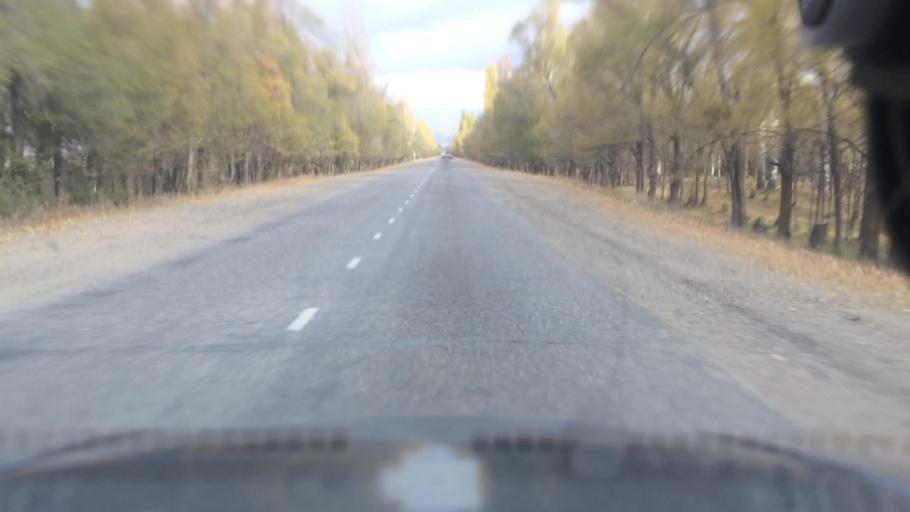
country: KG
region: Ysyk-Koel
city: Tyup
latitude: 42.6311
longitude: 78.3604
